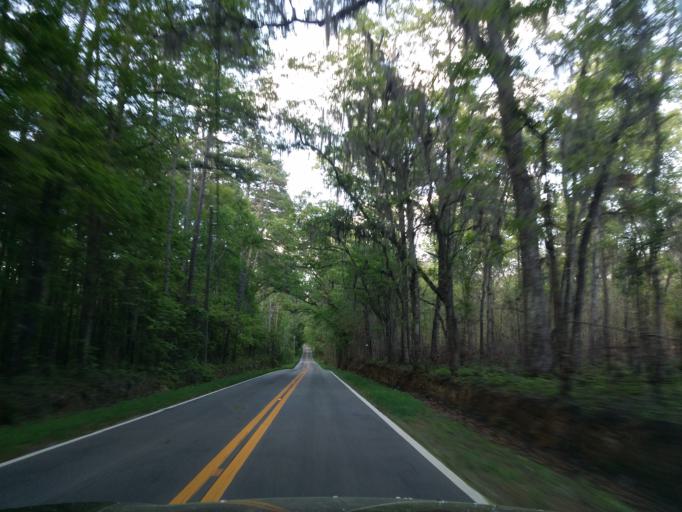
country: US
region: Florida
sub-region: Leon County
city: Tallahassee
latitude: 30.5091
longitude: -84.1473
